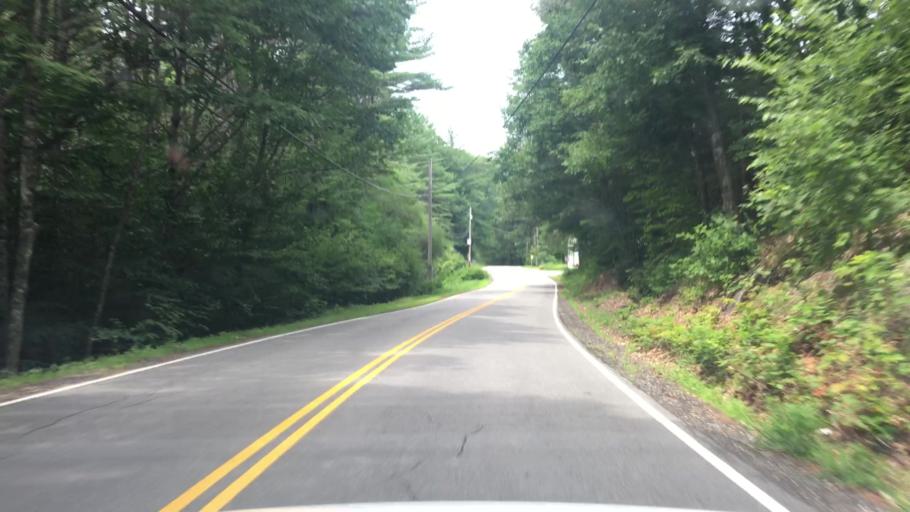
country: US
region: New Hampshire
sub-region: Grafton County
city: Rumney
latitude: 43.7997
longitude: -71.7989
